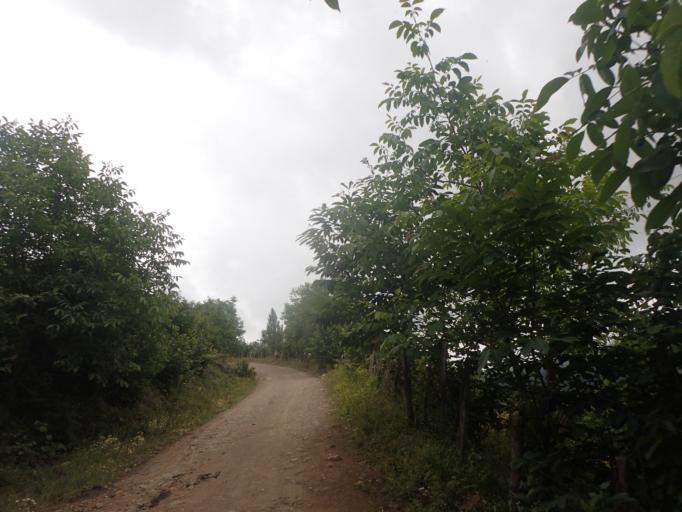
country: TR
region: Ordu
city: Akkus
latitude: 40.8705
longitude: 37.0084
